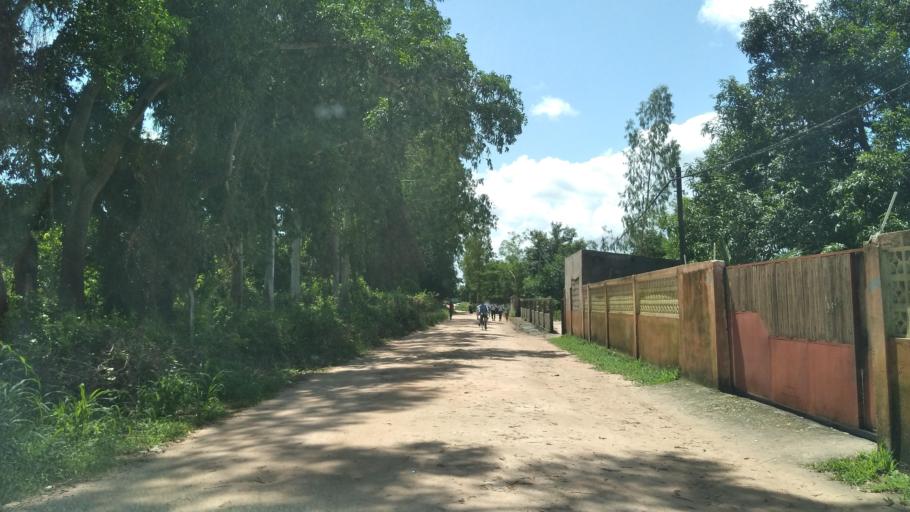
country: MZ
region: Zambezia
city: Quelimane
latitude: -17.6005
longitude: 36.8102
